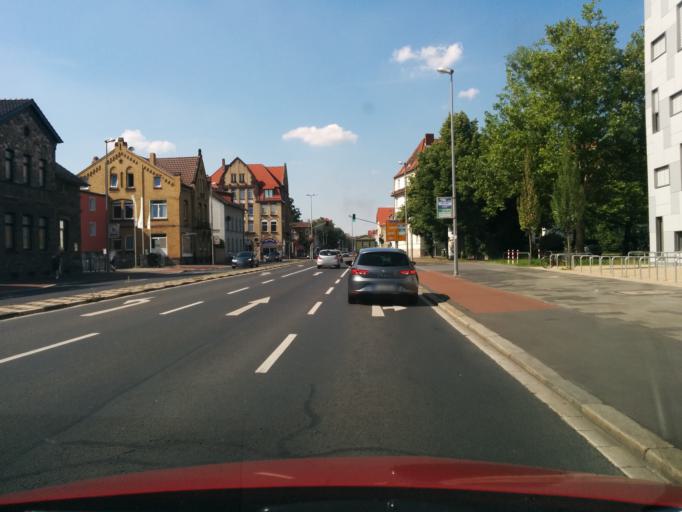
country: DE
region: Lower Saxony
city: Goettingen
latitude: 51.5413
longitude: 9.9331
